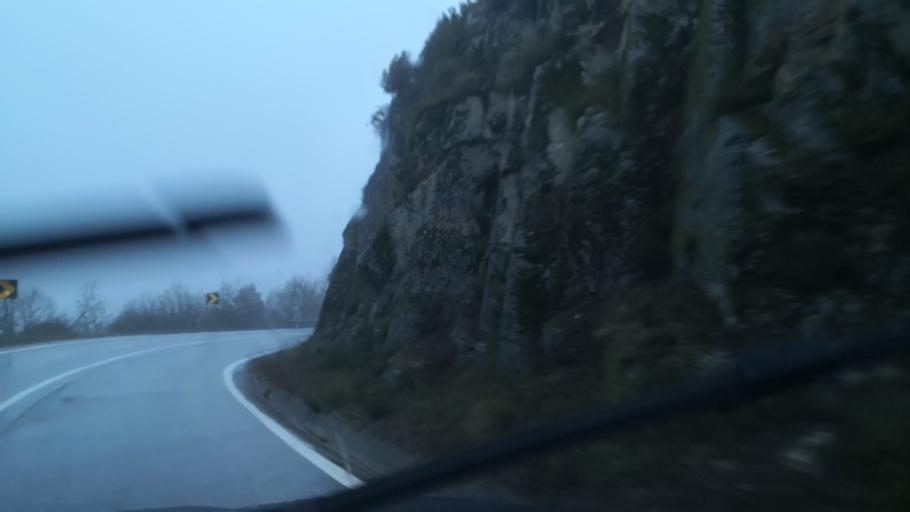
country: PT
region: Vila Real
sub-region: Vila Pouca de Aguiar
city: Vila Pouca de Aguiar
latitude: 41.4973
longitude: -7.6252
